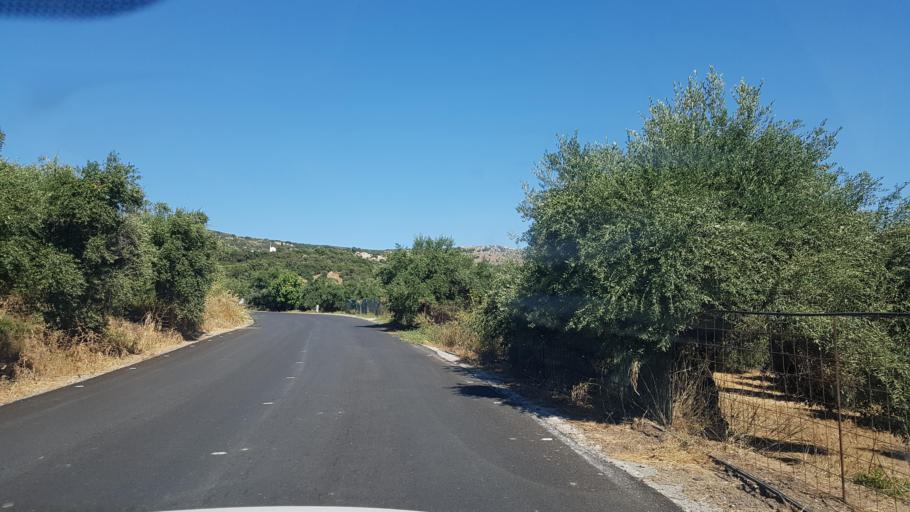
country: GR
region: Crete
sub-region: Nomos Chanias
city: Kissamos
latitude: 35.4950
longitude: 23.7200
